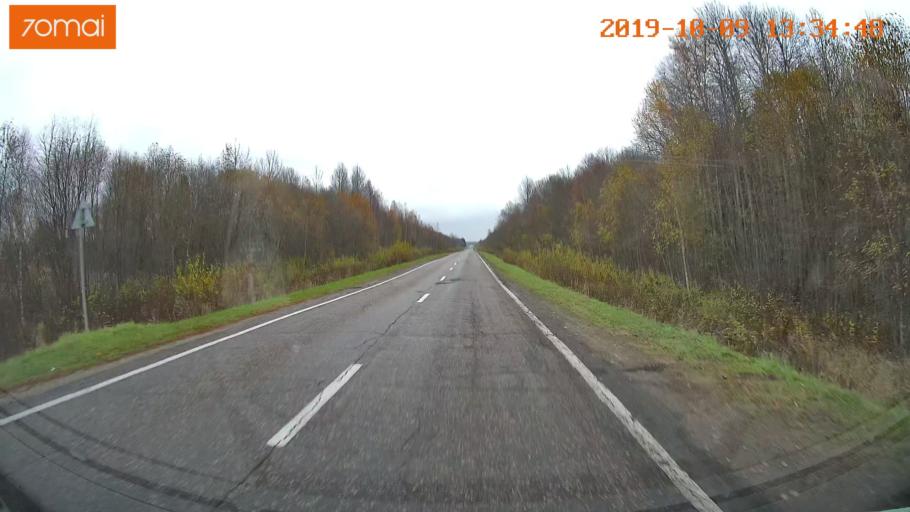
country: RU
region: Jaroslavl
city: Lyubim
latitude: 58.3320
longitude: 41.0662
